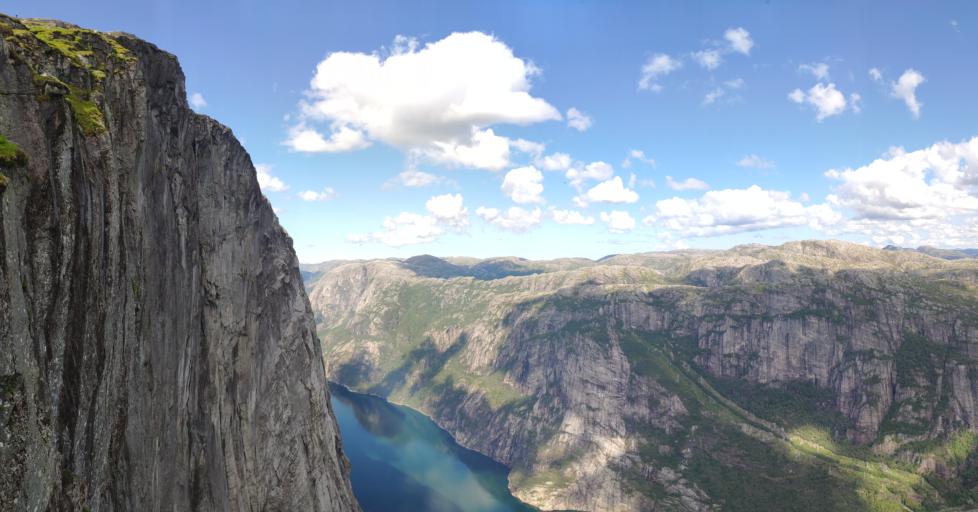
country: NO
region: Vest-Agder
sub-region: Sirdal
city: Tonstad
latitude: 59.0427
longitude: 6.6277
